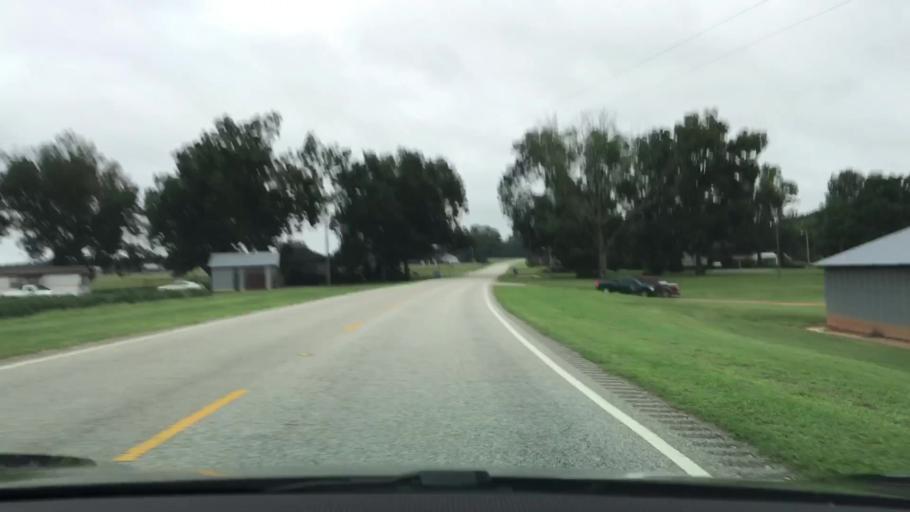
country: US
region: Alabama
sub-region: Coffee County
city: Elba
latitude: 31.3271
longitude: -86.1336
